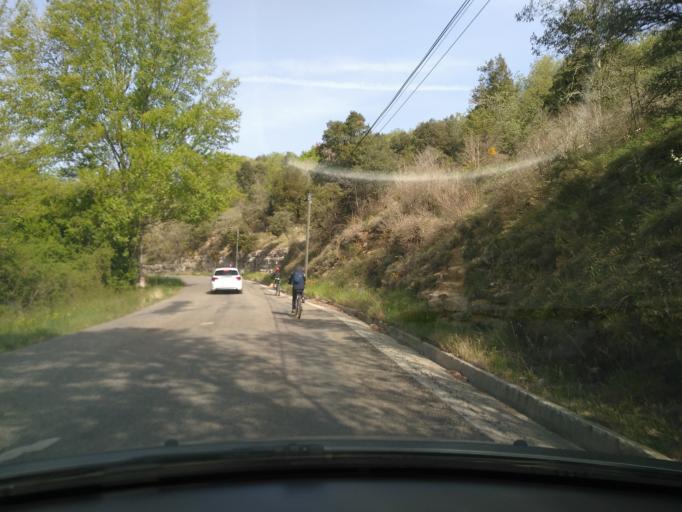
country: FR
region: Rhone-Alpes
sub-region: Departement de l'Ardeche
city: Ruoms
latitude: 44.4480
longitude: 4.3613
